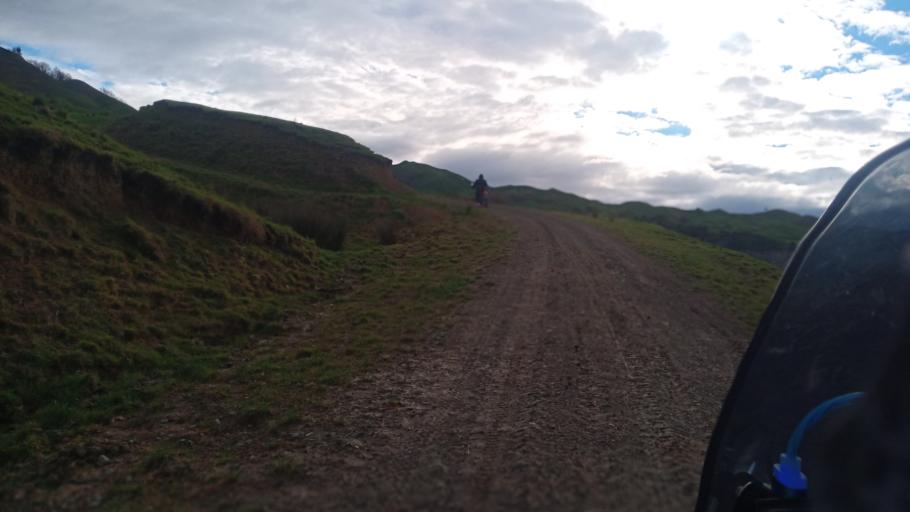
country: NZ
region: Gisborne
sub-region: Gisborne District
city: Gisborne
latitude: -38.3488
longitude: 177.9344
